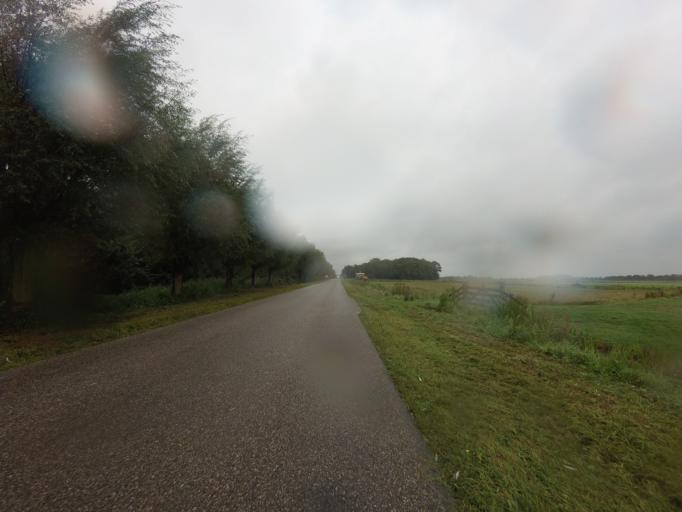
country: NL
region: Friesland
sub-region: Gemeente Tytsjerksteradiel
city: Garyp
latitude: 53.1337
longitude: 5.9556
